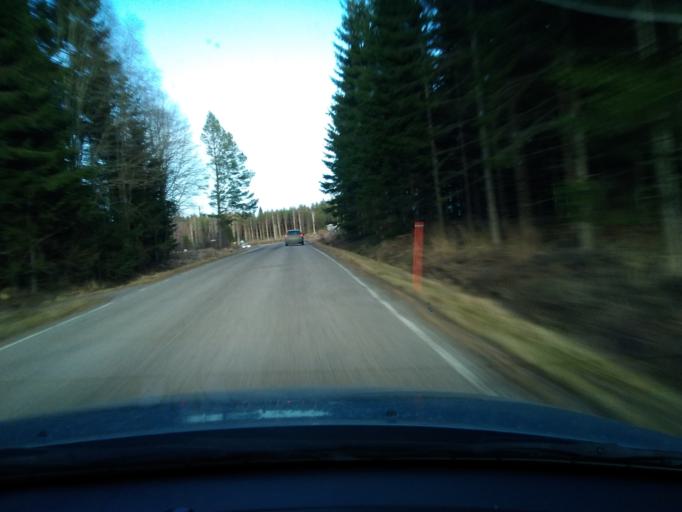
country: FI
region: Haeme
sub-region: Haemeenlinna
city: Renko
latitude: 60.7685
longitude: 24.2220
